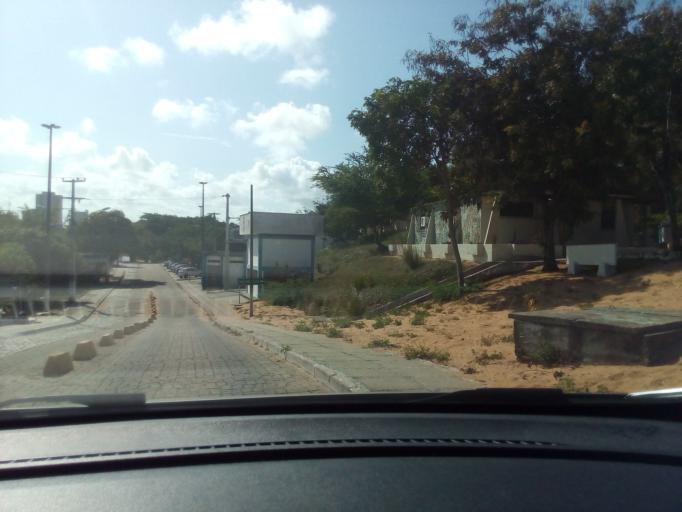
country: BR
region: Rio Grande do Norte
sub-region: Natal
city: Natal
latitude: -5.8385
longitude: -35.1995
